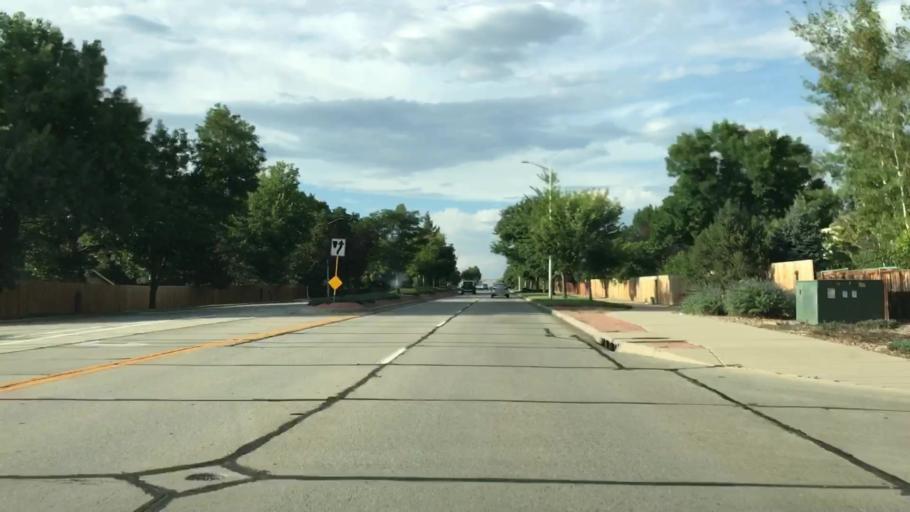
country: US
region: Colorado
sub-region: Boulder County
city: Longmont
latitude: 40.1995
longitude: -105.1309
